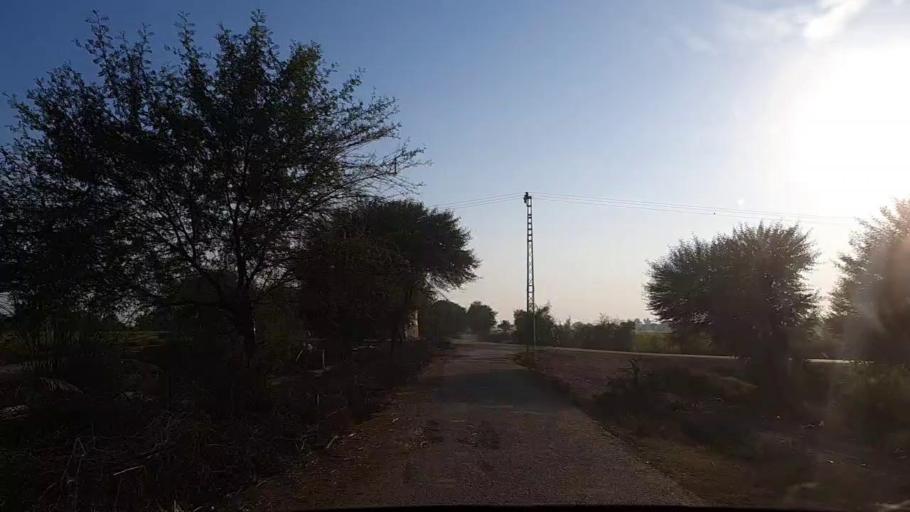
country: PK
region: Sindh
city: Sobhadero
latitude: 27.4006
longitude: 68.3892
